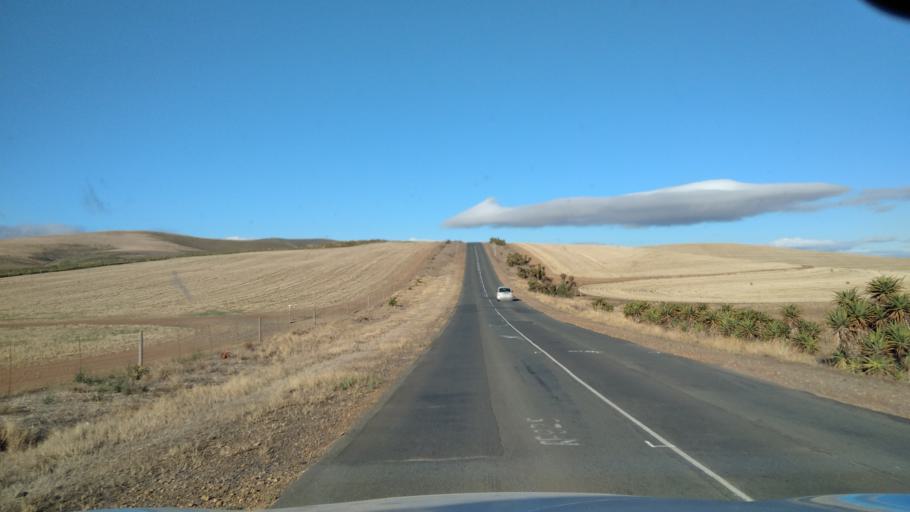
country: ZA
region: Western Cape
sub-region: Overberg District Municipality
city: Caledon
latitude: -34.1713
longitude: 19.2861
